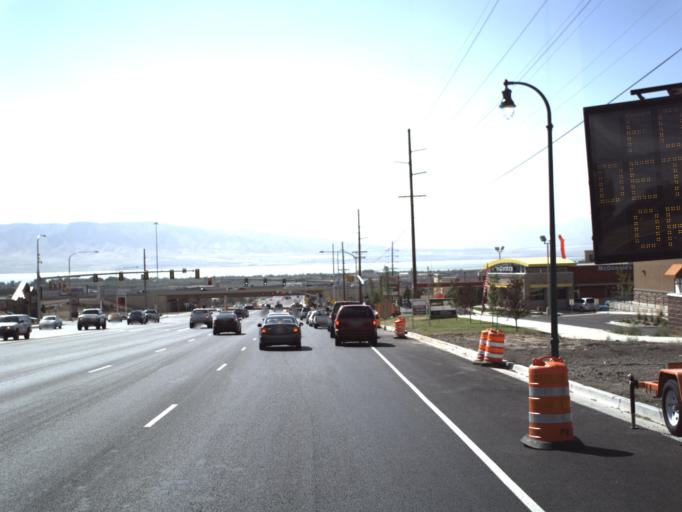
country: US
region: Utah
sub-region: Utah County
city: Orem
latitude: 40.3121
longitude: -111.7183
